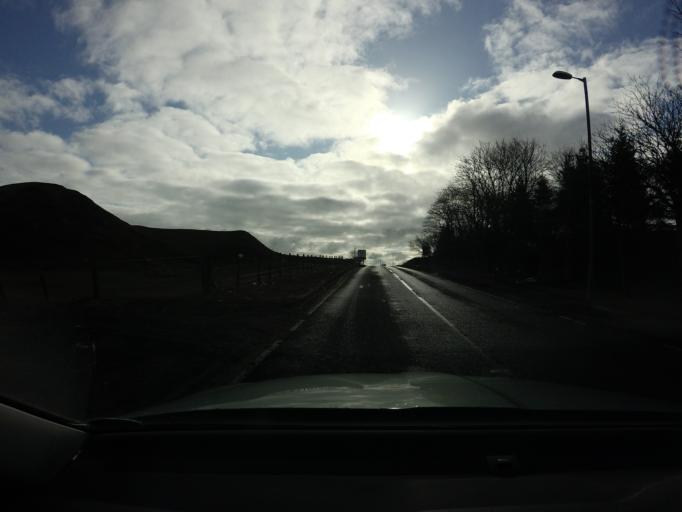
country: GB
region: Scotland
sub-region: South Lanarkshire
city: Forth
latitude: 55.7019
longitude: -3.6937
